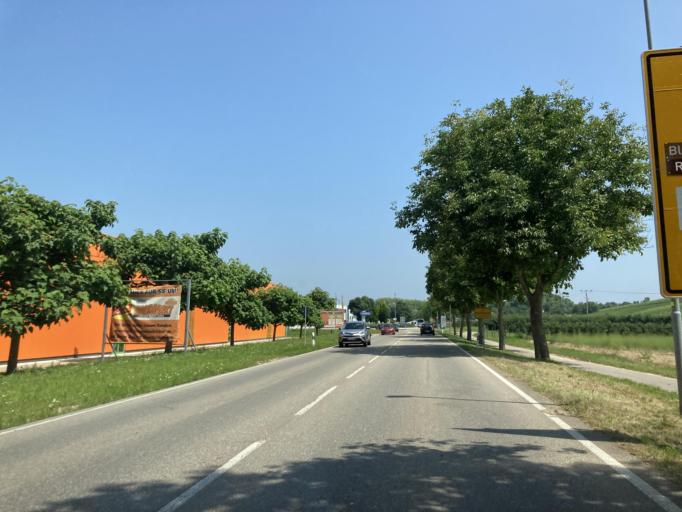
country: DE
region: Baden-Wuerttemberg
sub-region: Freiburg Region
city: Auggen
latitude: 47.8053
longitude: 7.6040
